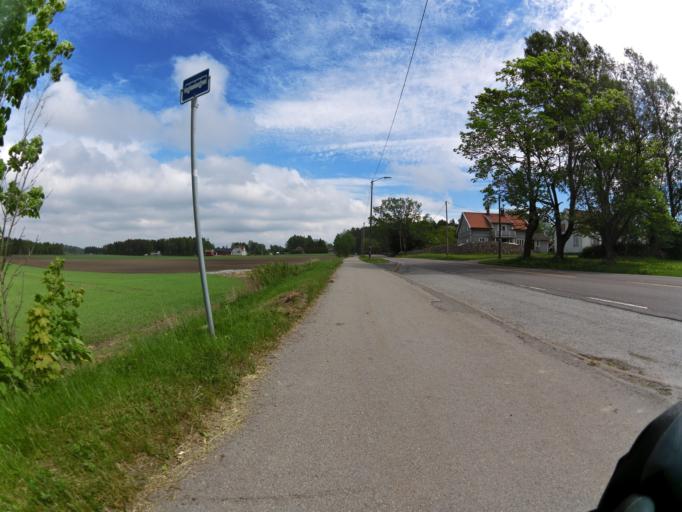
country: NO
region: Ostfold
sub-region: Rade
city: Karlshus
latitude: 59.3457
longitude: 10.8999
